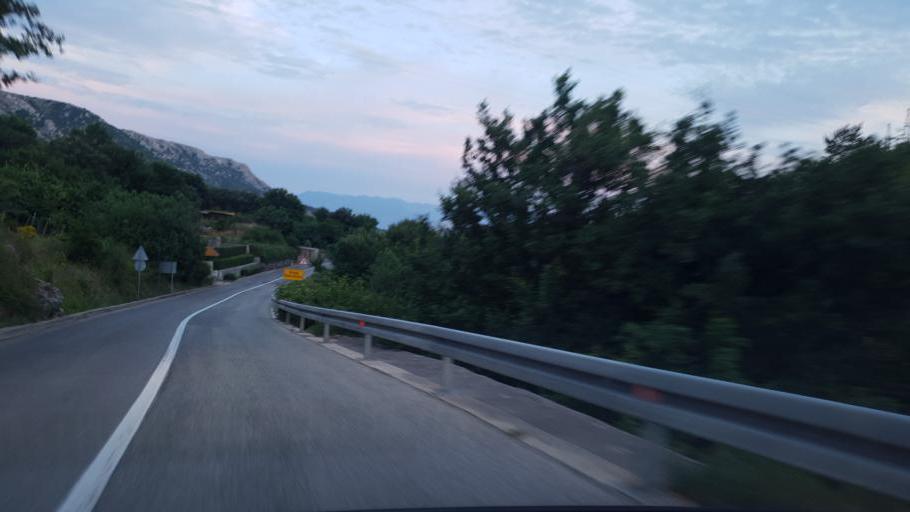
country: HR
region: Primorsko-Goranska
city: Punat
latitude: 45.0007
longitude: 14.7078
